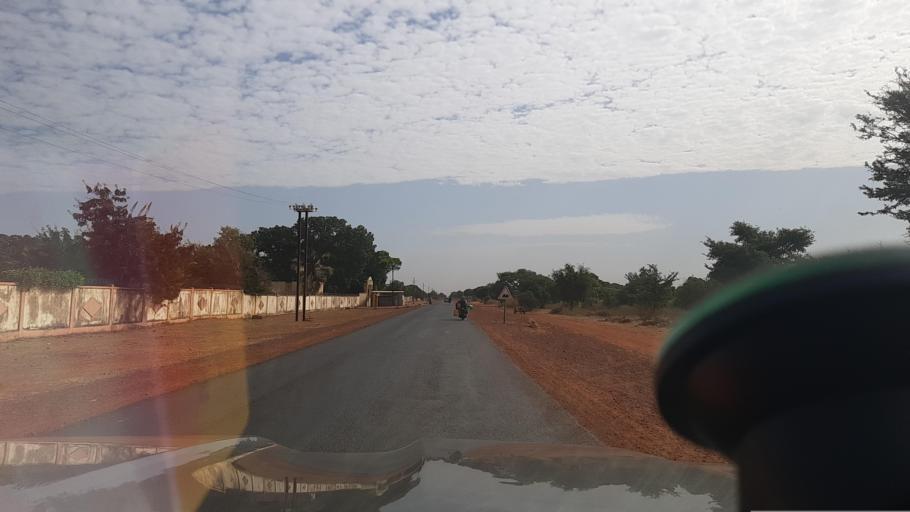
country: ML
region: Segou
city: Segou
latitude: 13.4972
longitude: -6.1628
